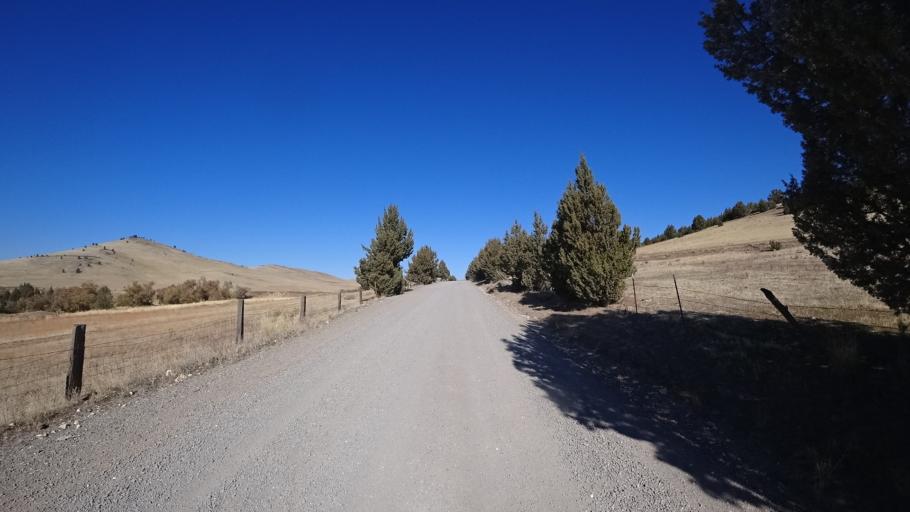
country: US
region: California
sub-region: Siskiyou County
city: Montague
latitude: 41.7294
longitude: -122.3695
